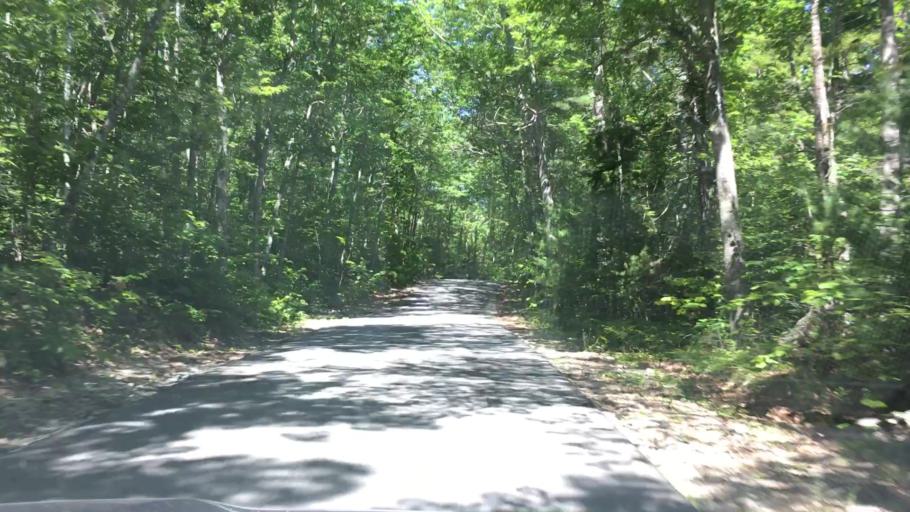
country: US
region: Maine
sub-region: Hancock County
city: Sedgwick
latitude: 44.3330
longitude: -68.6590
